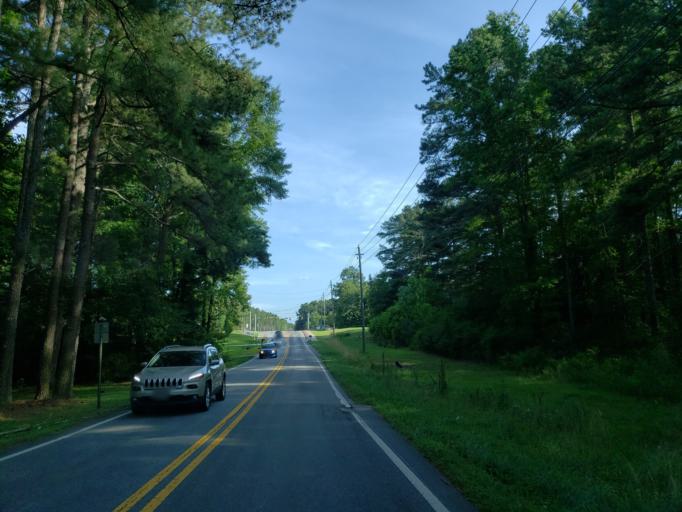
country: US
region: Georgia
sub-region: Cobb County
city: Powder Springs
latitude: 33.9048
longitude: -84.7065
